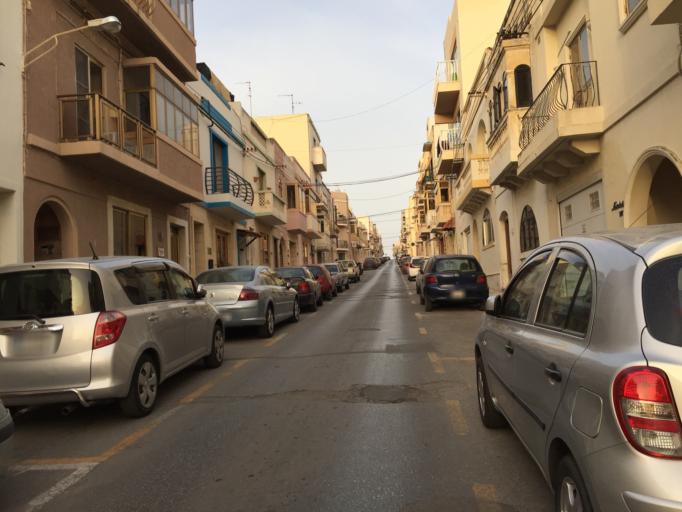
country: MT
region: Il-Fgura
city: Fgura
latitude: 35.8746
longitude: 14.5163
